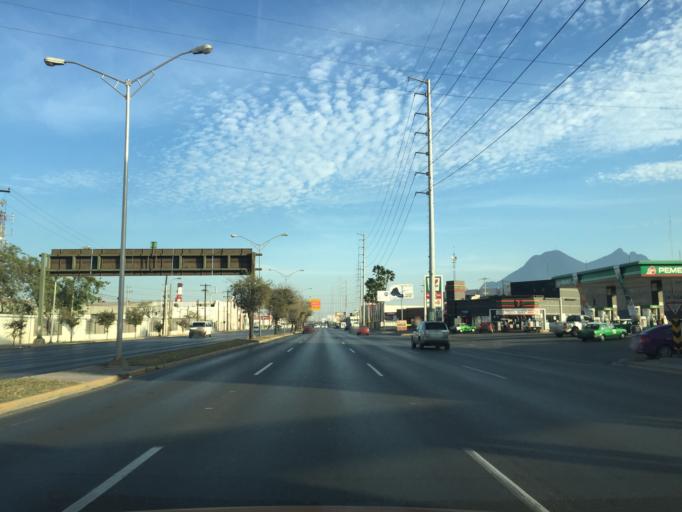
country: MX
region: Nuevo Leon
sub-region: San Nicolas de los Garza
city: San Nicolas de los Garza
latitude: 25.7193
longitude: -100.2889
